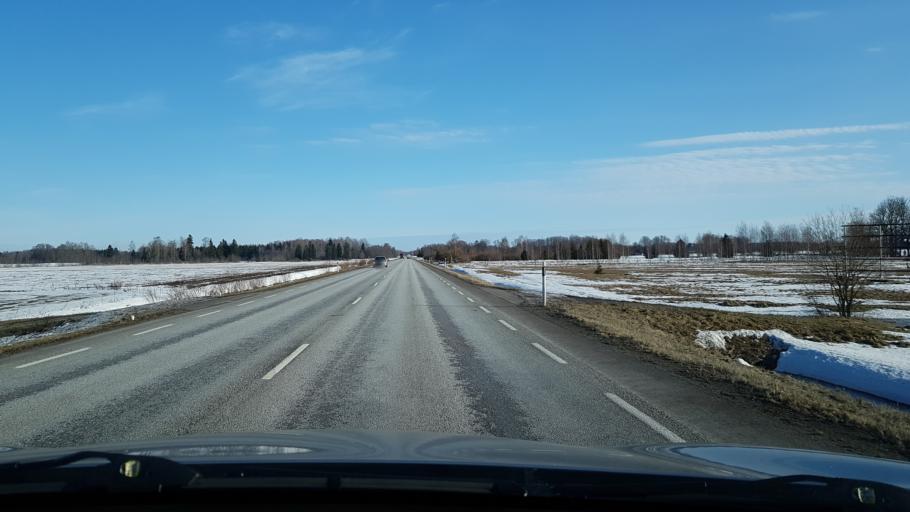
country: EE
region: Viljandimaa
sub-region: Vohma linn
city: Vohma
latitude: 58.6845
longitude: 25.6886
